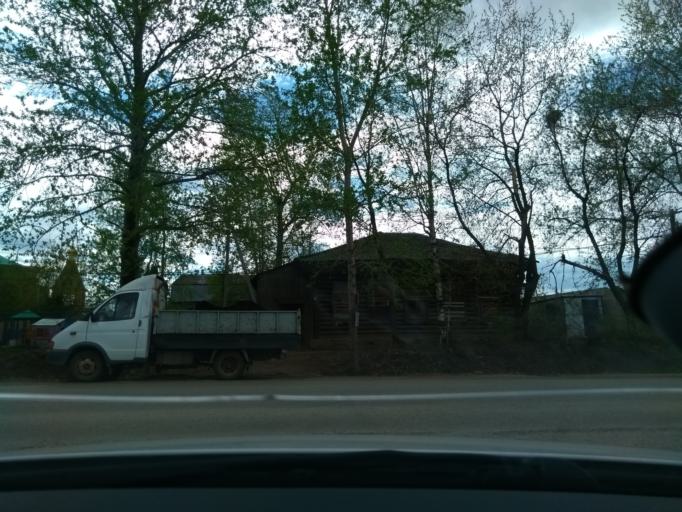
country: RU
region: Perm
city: Lobanovo
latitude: 57.8616
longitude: 56.3007
